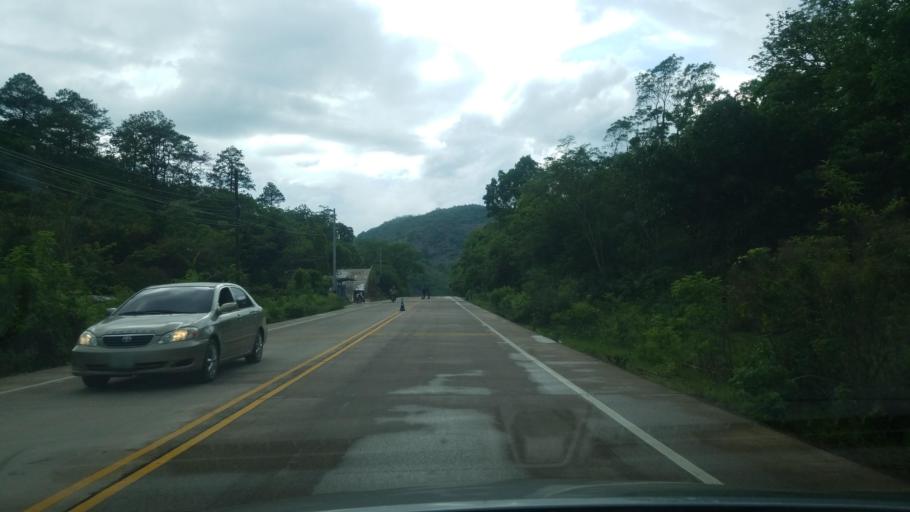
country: HN
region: Copan
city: Copan
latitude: 14.8473
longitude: -89.1913
